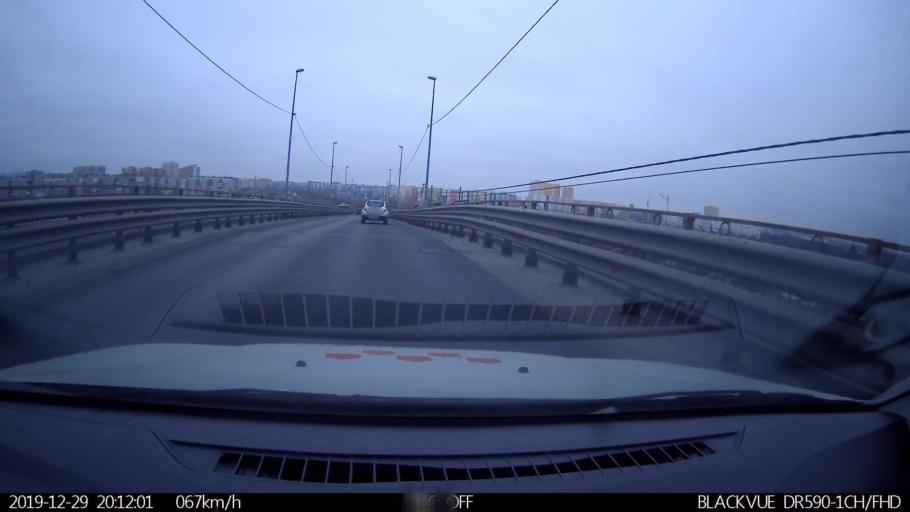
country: RU
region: Nizjnij Novgorod
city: Nizhniy Novgorod
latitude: 56.3503
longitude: 43.9225
